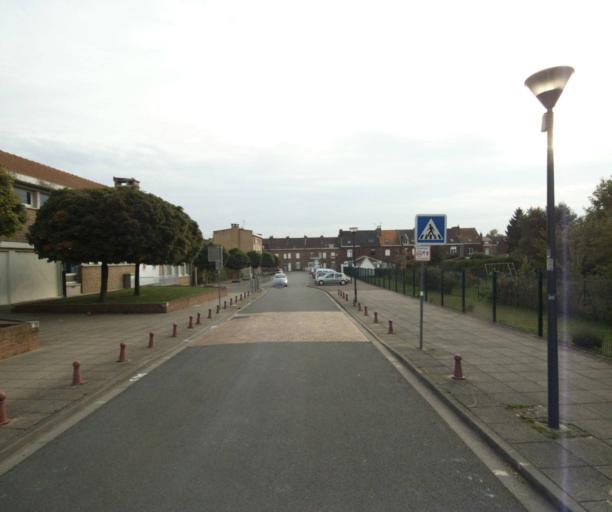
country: FR
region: Nord-Pas-de-Calais
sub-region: Departement du Nord
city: Seclin
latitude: 50.5476
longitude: 3.0423
